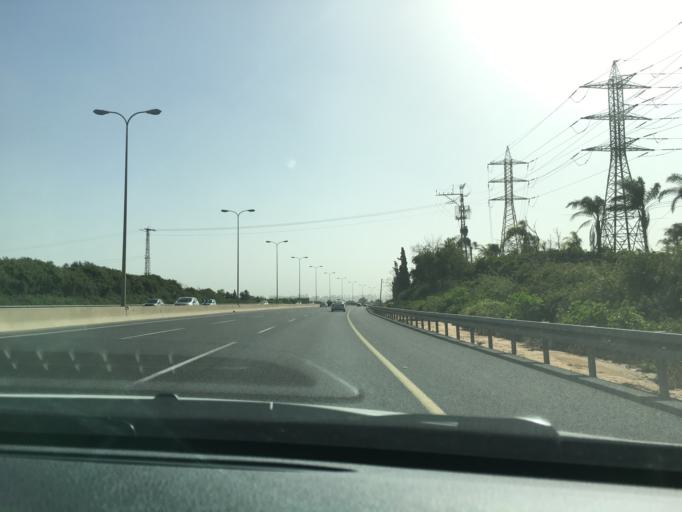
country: IL
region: Central District
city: Hod HaSharon
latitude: 32.1470
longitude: 34.8735
